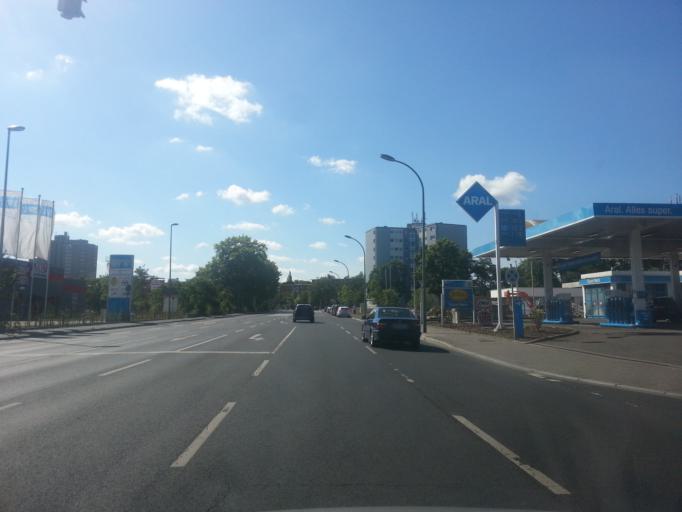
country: DE
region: Hesse
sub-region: Regierungsbezirk Darmstadt
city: Offenbach
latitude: 50.0871
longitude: 8.7703
